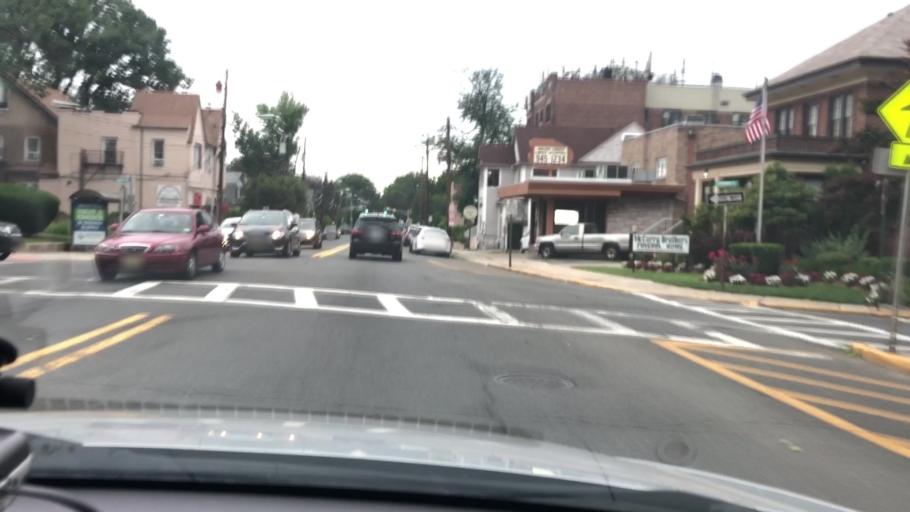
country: US
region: New Jersey
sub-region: Bergen County
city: Cliffside Park
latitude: 40.8312
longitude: -73.9851
